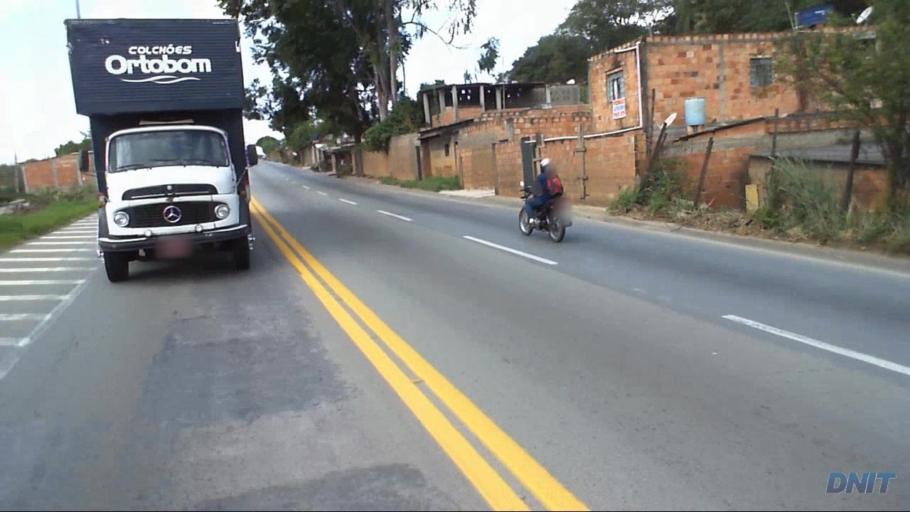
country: BR
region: Minas Gerais
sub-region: Santa Luzia
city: Santa Luzia
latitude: -19.8234
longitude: -43.8299
